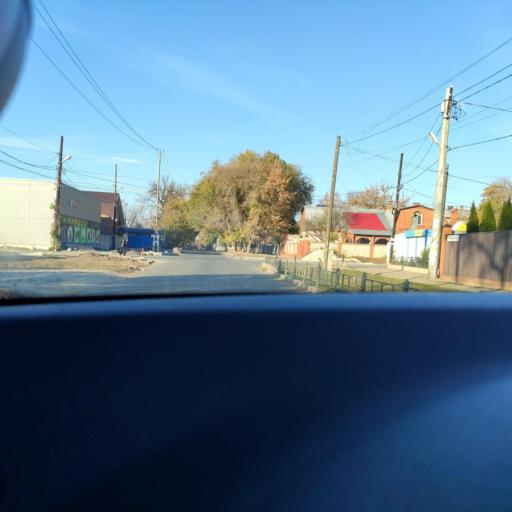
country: RU
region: Samara
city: Petra-Dubrava
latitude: 53.2479
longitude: 50.3282
